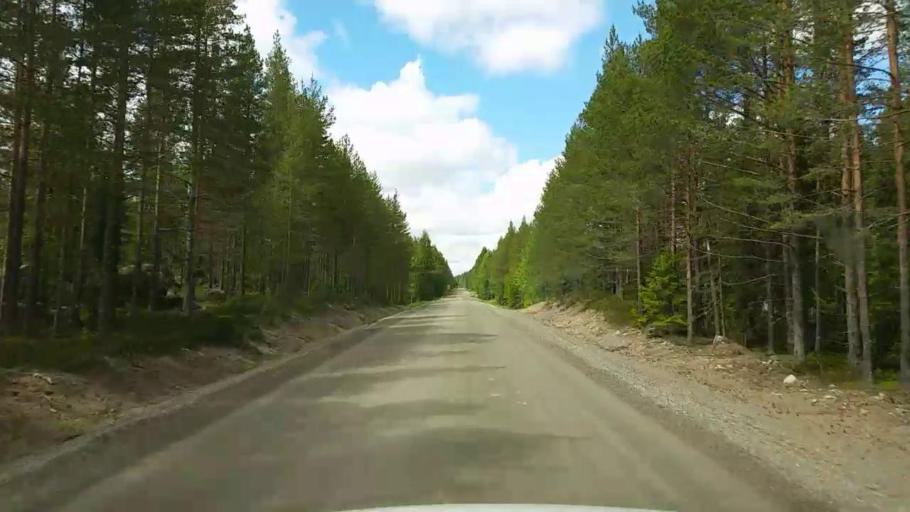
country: SE
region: Gaevleborg
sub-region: Bollnas Kommun
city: Vittsjo
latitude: 61.0347
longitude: 16.3651
